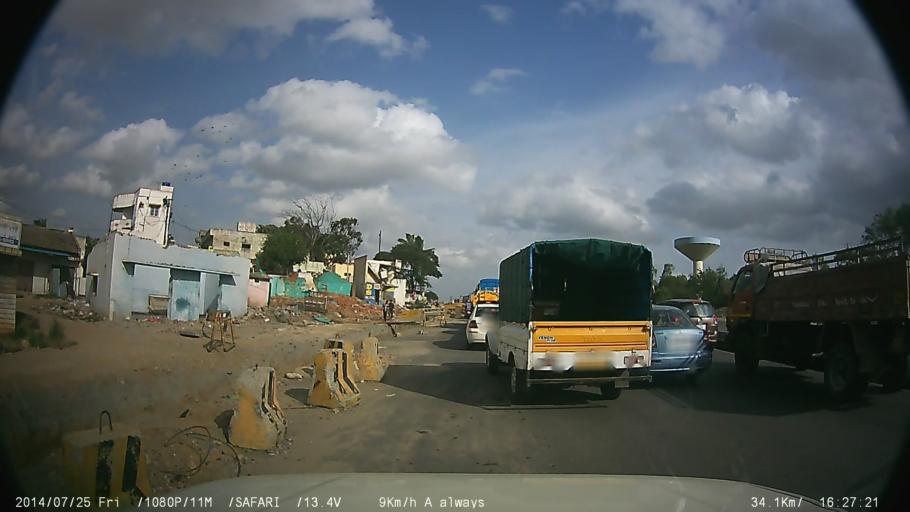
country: IN
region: Tamil Nadu
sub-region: Krishnagiri
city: Hosur
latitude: 12.7677
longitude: 77.7892
